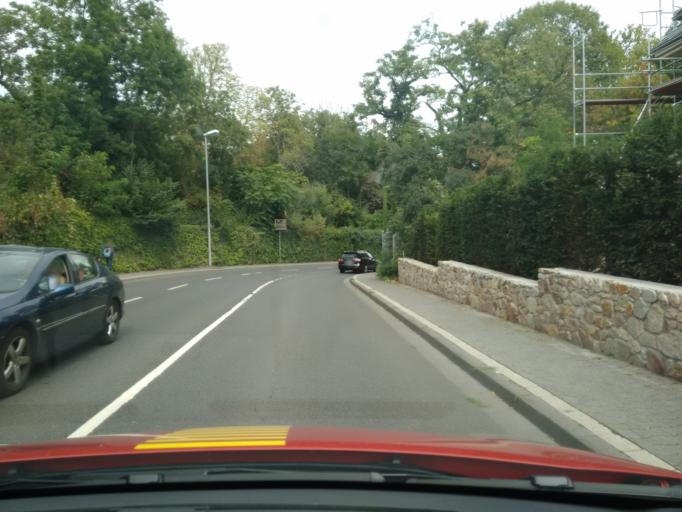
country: DE
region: Rheinland-Pfalz
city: Mainz
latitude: 49.9931
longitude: 8.2709
